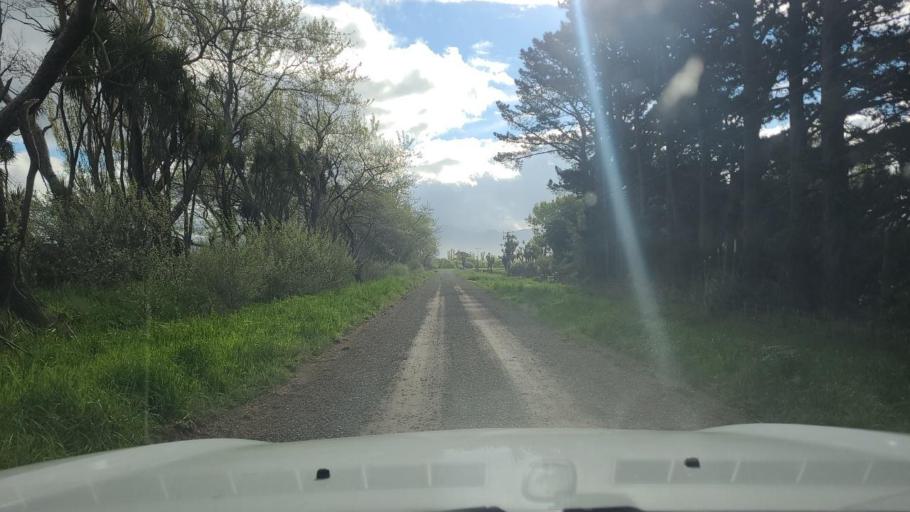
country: NZ
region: Wellington
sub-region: Upper Hutt City
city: Upper Hutt
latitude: -41.2920
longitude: 175.2191
